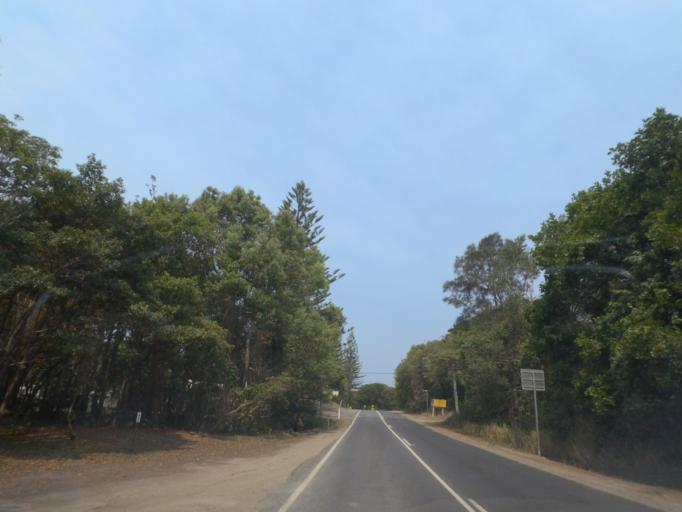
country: AU
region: New South Wales
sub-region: Tweed
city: Pottsville Beach
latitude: -28.4569
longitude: 153.5515
